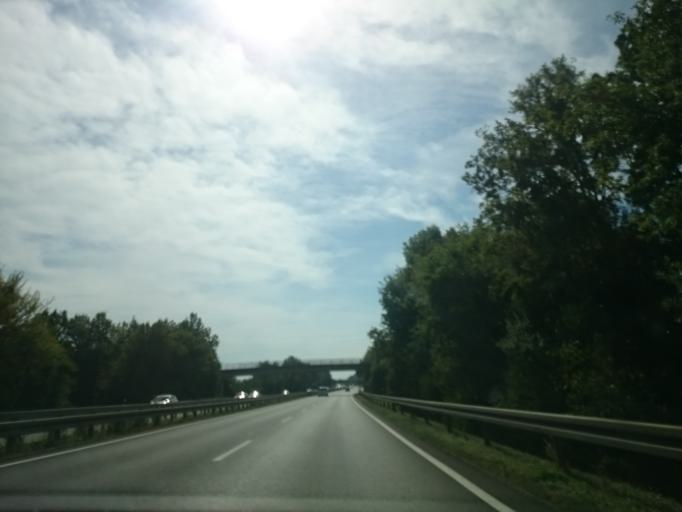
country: DE
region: Bavaria
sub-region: Swabia
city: Donauwoerth
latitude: 48.7083
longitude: 10.8042
